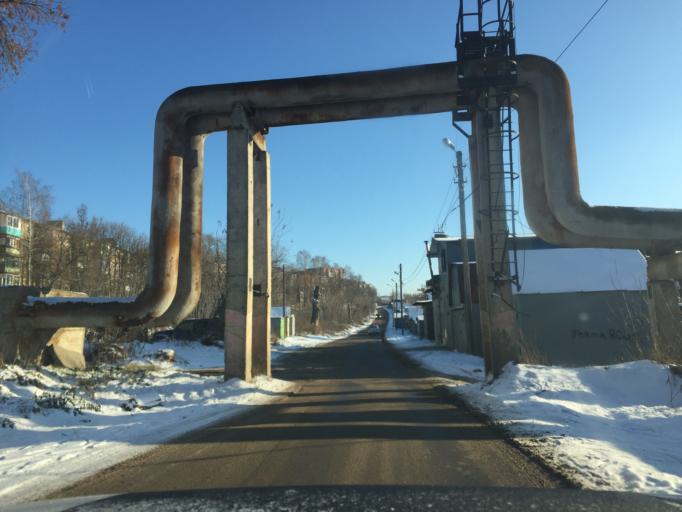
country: RU
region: Tula
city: Tula
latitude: 54.1912
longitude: 37.6784
